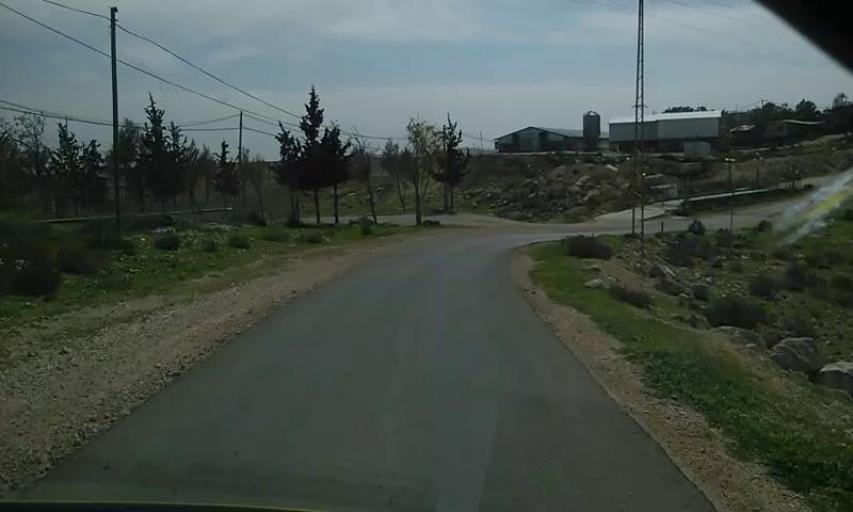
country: PS
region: West Bank
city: Khallat al Mayyah
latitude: 31.4346
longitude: 35.1883
